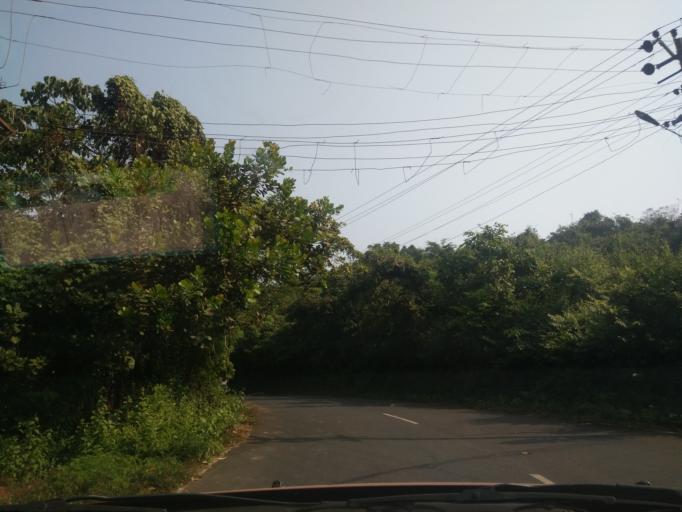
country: IN
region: Goa
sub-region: North Goa
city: Palle
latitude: 15.4727
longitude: 74.1083
